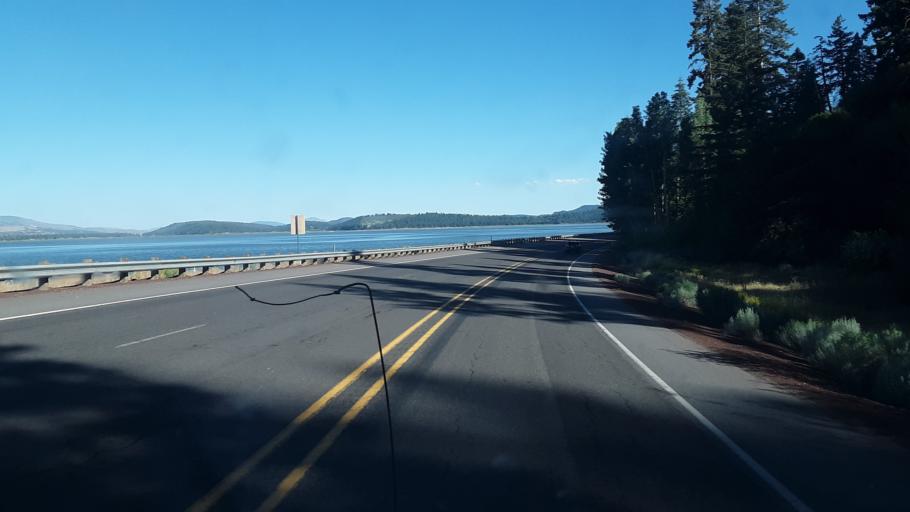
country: US
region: Oregon
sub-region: Klamath County
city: Klamath Falls
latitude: 42.3206
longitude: -121.9436
